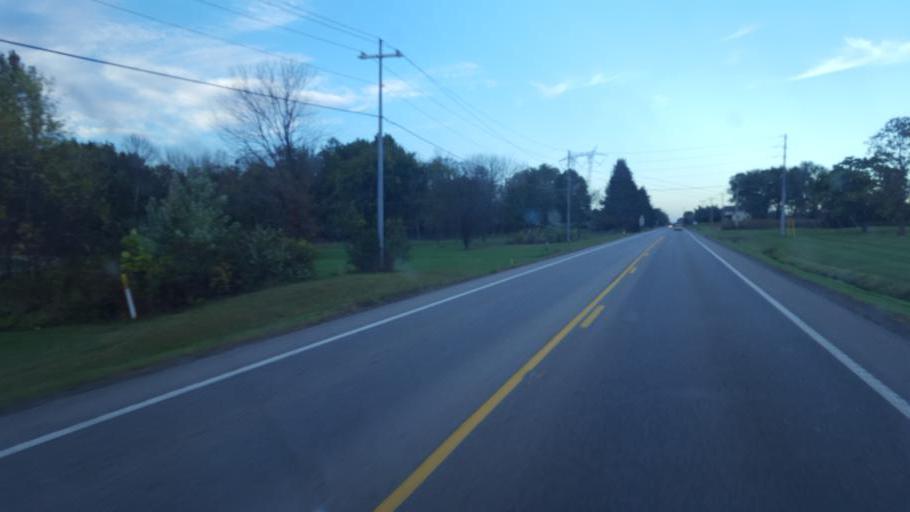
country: US
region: Ohio
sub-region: Licking County
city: Johnstown
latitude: 40.1897
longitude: -82.6073
